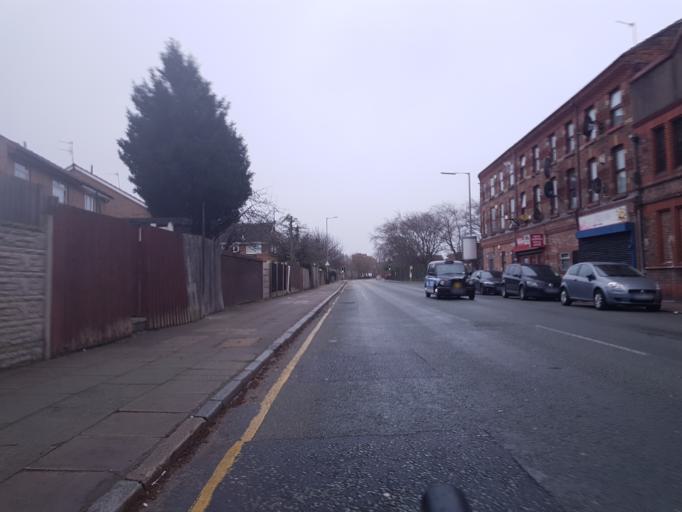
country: GB
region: England
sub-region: Liverpool
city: Liverpool
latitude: 53.4347
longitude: -2.9758
